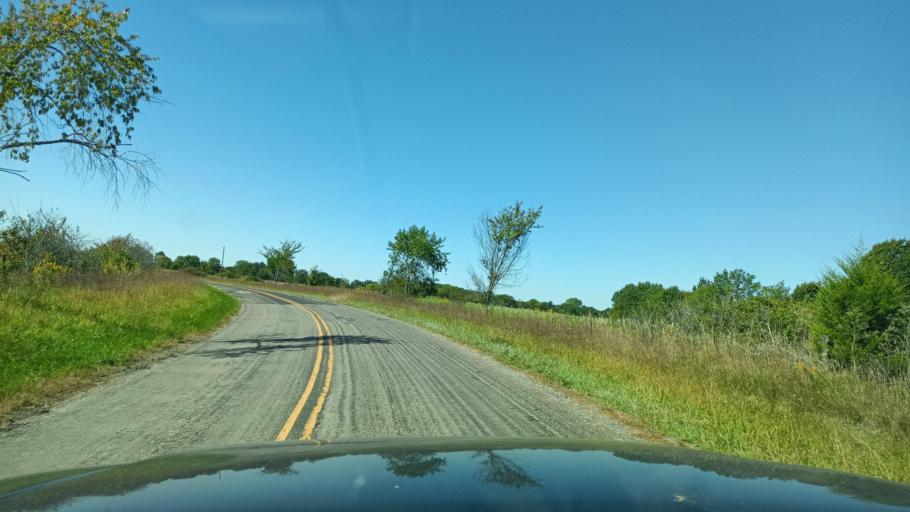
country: US
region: Missouri
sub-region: Scotland County
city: Memphis
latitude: 40.3540
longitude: -92.2711
